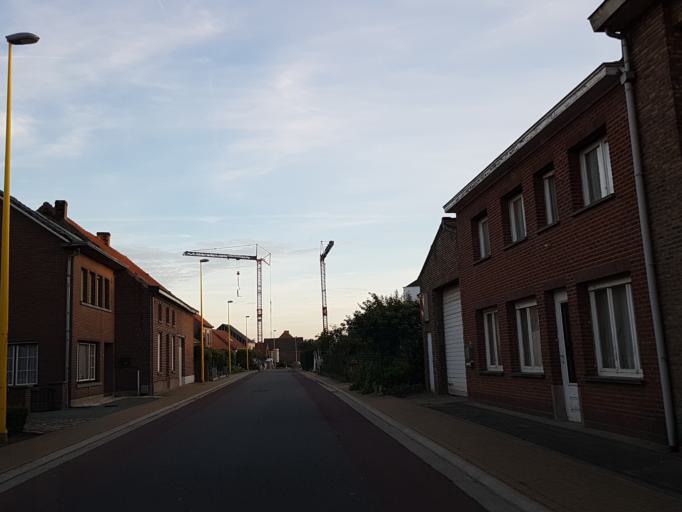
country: BE
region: Flanders
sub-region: Provincie Vlaams-Brabant
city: Meise
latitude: 50.9611
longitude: 4.2899
